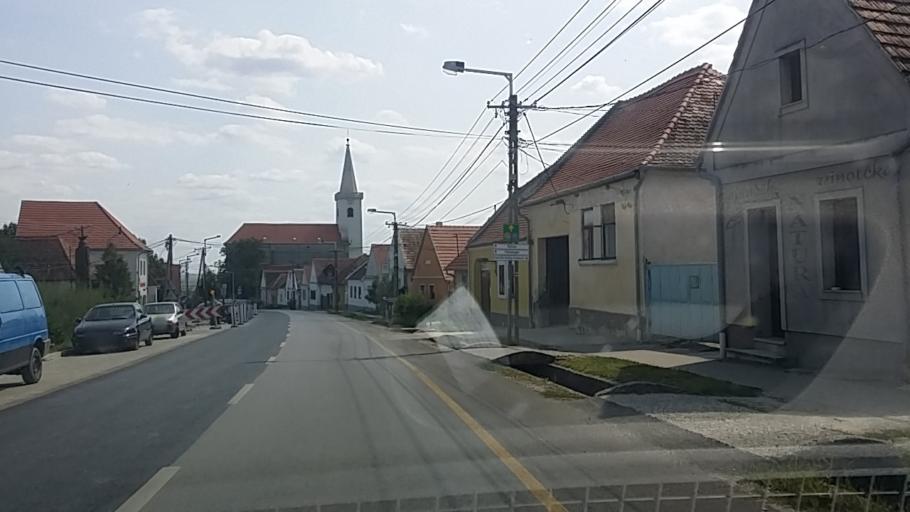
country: HU
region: Gyor-Moson-Sopron
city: Fertorakos
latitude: 47.7206
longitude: 16.6501
